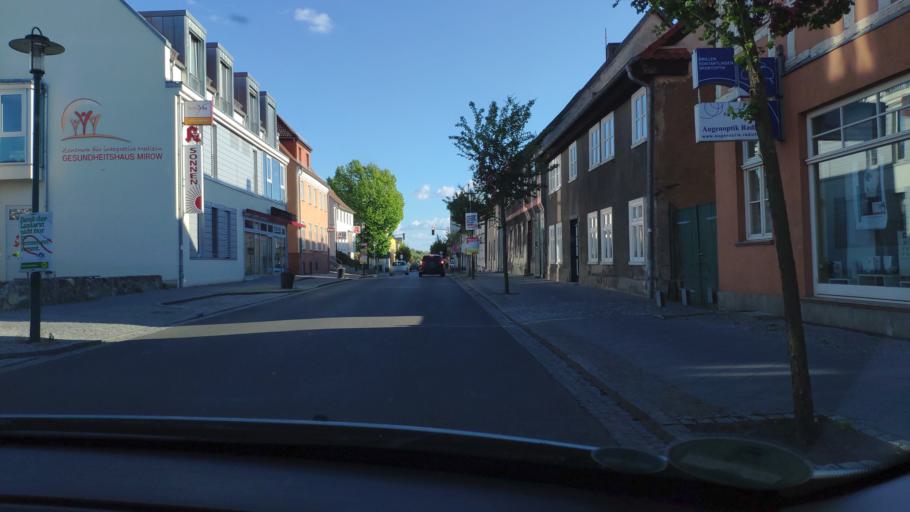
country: DE
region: Mecklenburg-Vorpommern
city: Rechlin
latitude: 53.2755
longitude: 12.8156
